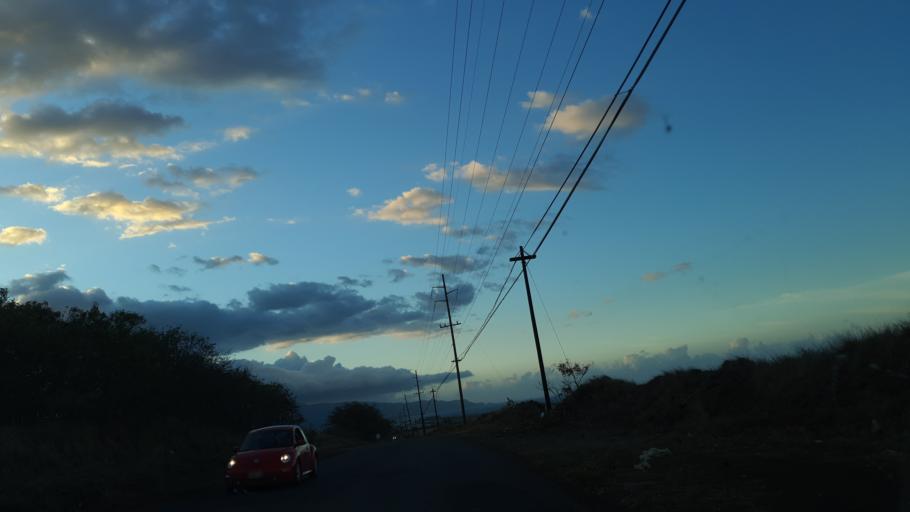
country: US
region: Hawaii
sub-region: Maui County
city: Kahului
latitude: 20.8594
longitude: -156.4255
